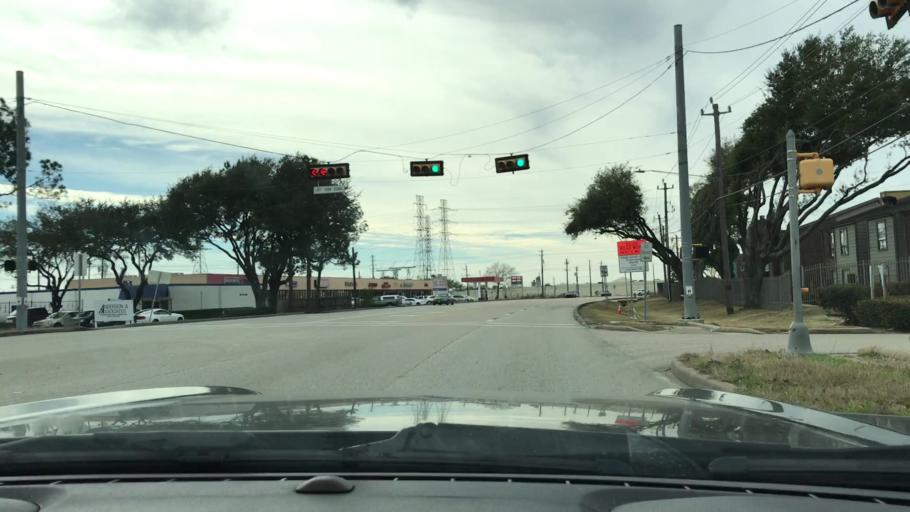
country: US
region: Texas
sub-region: Galveston County
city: Friendswood
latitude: 29.5902
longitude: -95.1810
